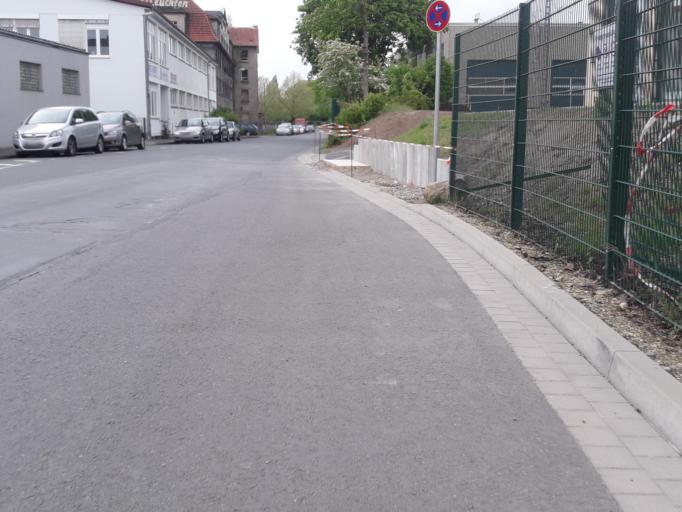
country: DE
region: North Rhine-Westphalia
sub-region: Regierungsbezirk Detmold
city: Detmold
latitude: 51.9410
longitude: 8.8703
